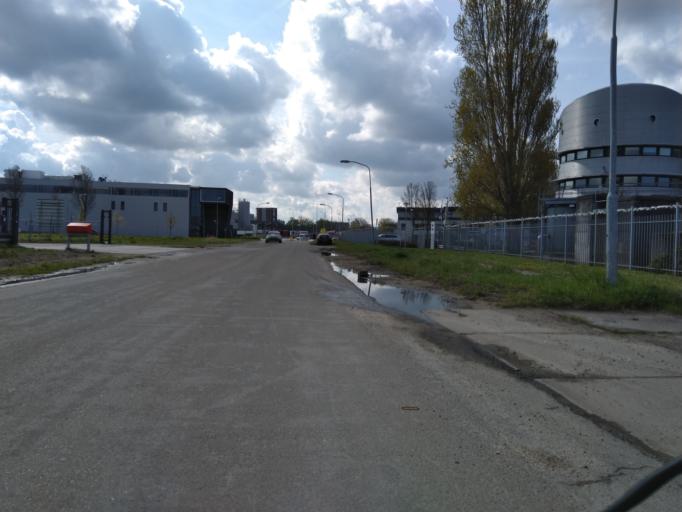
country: NL
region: North Holland
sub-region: Gemeente Haarlem
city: Haarlem
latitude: 52.3851
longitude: 4.6547
